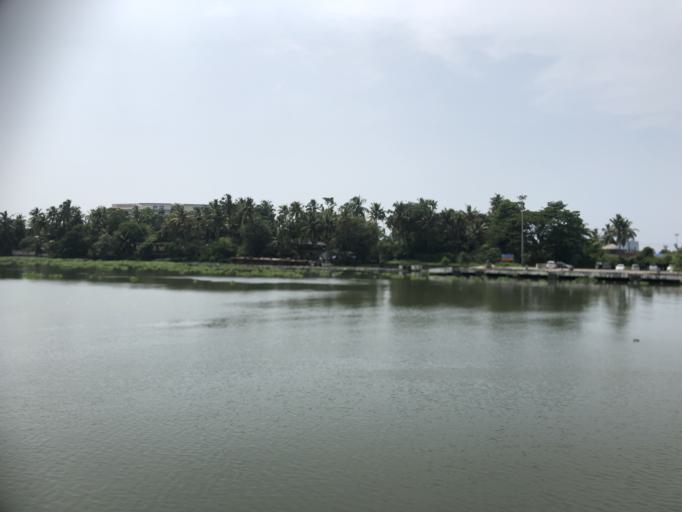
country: IN
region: Kerala
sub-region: Ernakulam
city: Cochin
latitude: 9.9913
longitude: 76.2678
